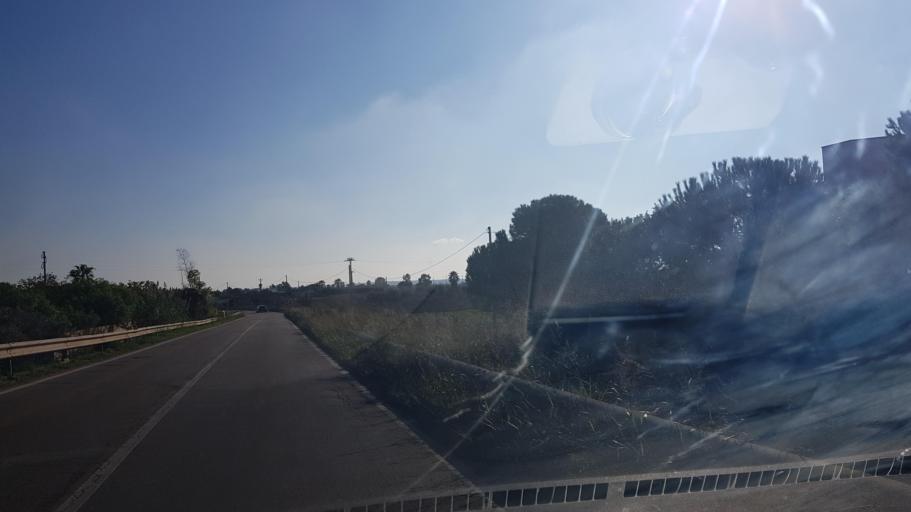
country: IT
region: Apulia
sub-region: Provincia di Lecce
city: Montesano Salentino
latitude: 39.9700
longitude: 18.3289
